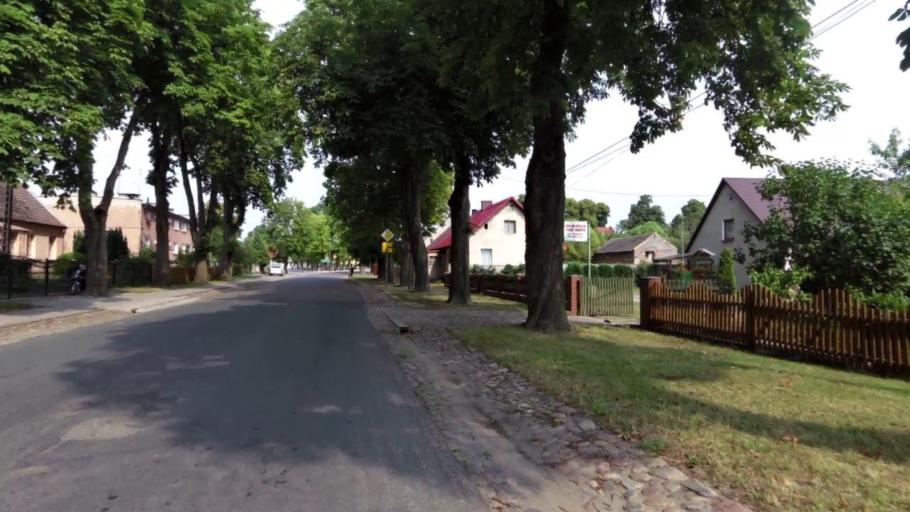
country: PL
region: West Pomeranian Voivodeship
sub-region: Powiat mysliborski
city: Debno
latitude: 52.8516
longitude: 14.6723
